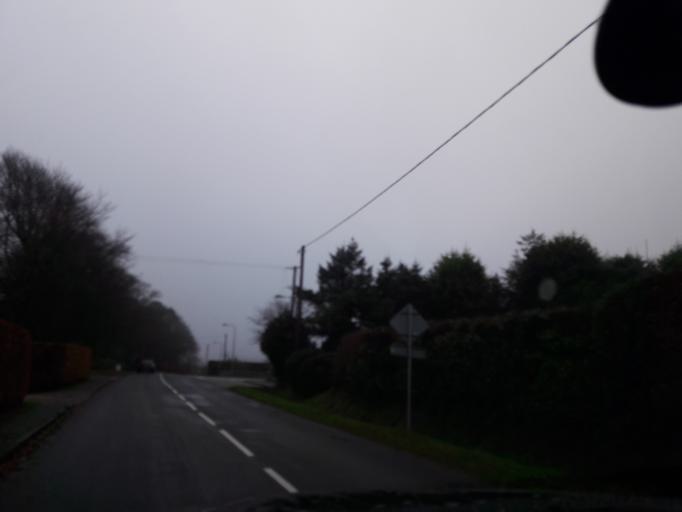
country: IE
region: Ulster
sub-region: County Donegal
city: Ramelton
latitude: 55.0333
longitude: -7.6472
